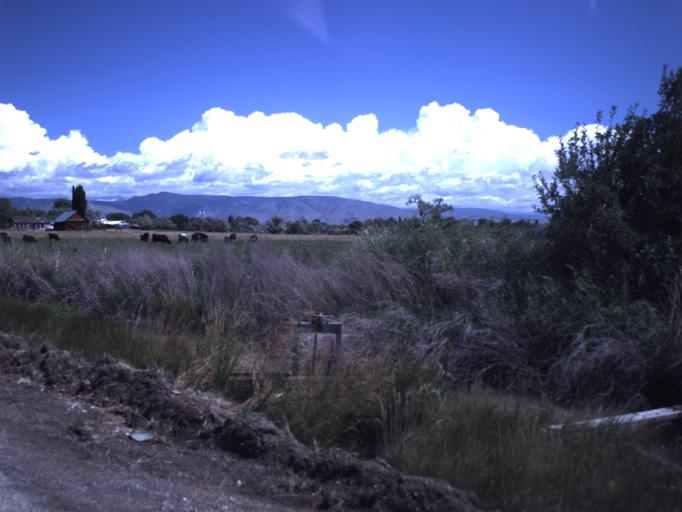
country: US
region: Utah
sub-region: Duchesne County
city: Roosevelt
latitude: 40.4223
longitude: -110.0300
